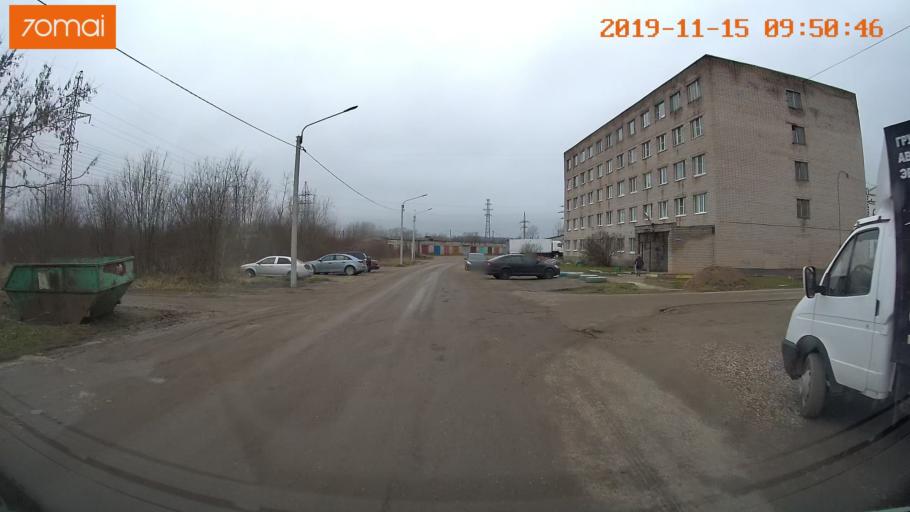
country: RU
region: Vologda
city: Sheksna
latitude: 59.2324
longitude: 38.5095
